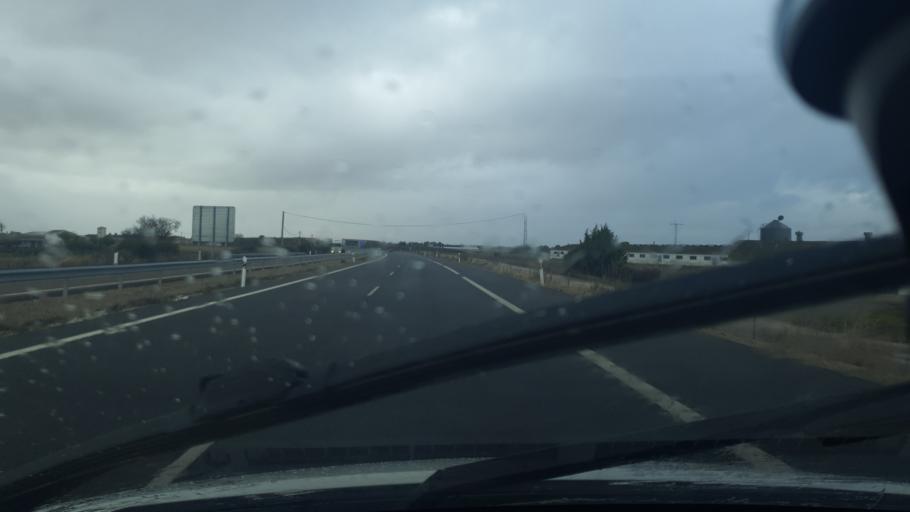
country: ES
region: Castille and Leon
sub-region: Provincia de Segovia
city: Cuellar
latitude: 41.4125
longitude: -4.3065
